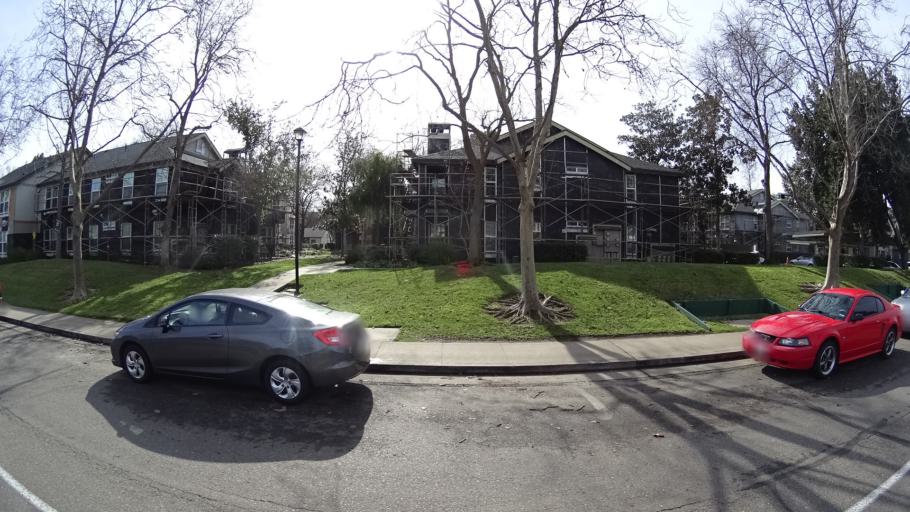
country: US
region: California
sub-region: Yolo County
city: Davis
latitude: 38.5399
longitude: -121.7283
